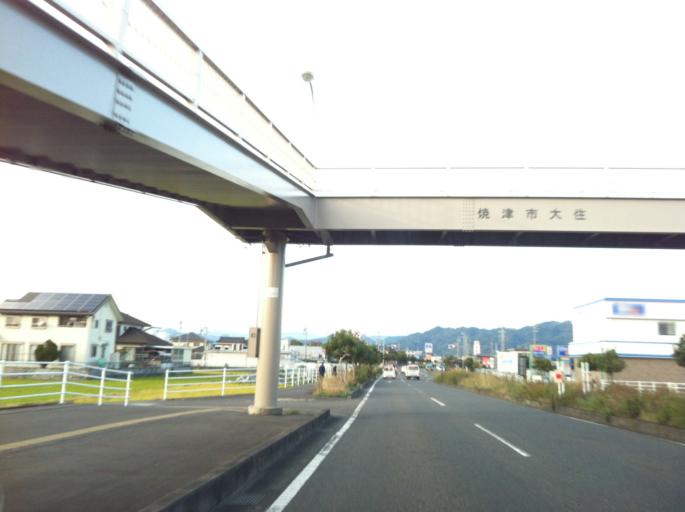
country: JP
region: Shizuoka
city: Yaizu
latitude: 34.8497
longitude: 138.2995
